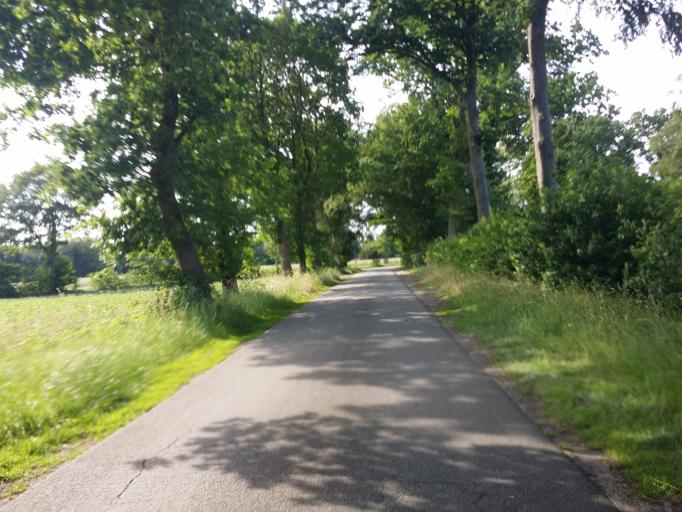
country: DE
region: Lower Saxony
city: Bockhorn
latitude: 53.3246
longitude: 8.0337
